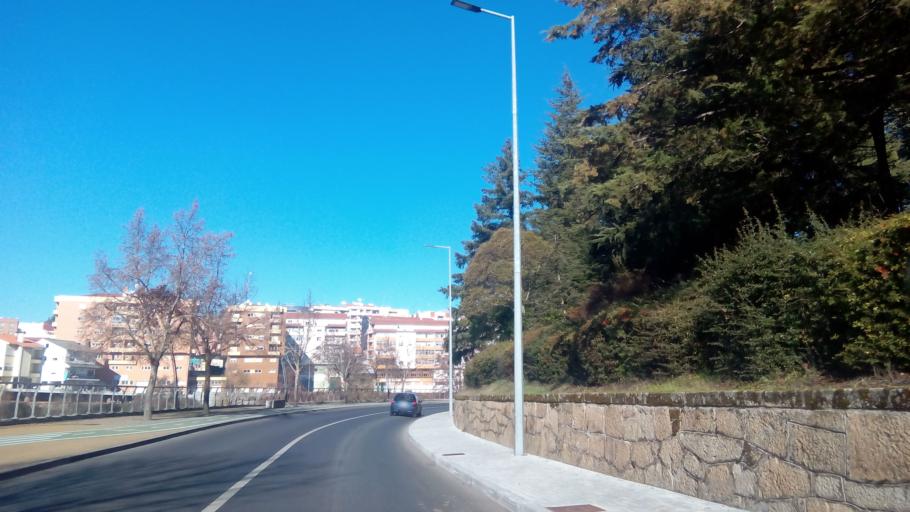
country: PT
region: Braganca
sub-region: Braganca Municipality
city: Braganca
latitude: 41.7987
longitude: -6.7623
